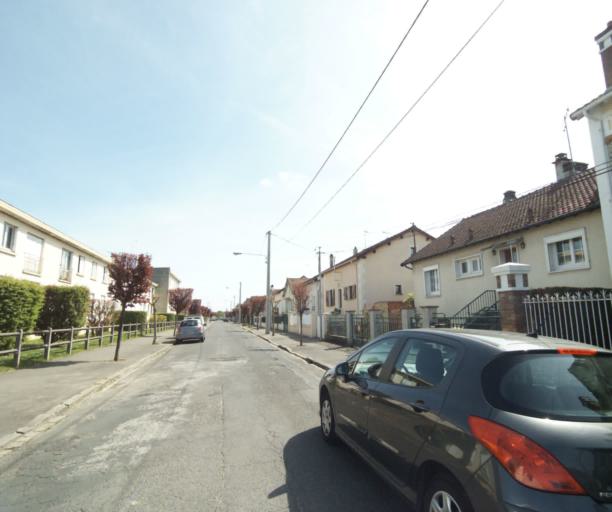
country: FR
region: Ile-de-France
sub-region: Departement de Seine-et-Marne
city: Nangis
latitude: 48.5578
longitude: 3.0195
